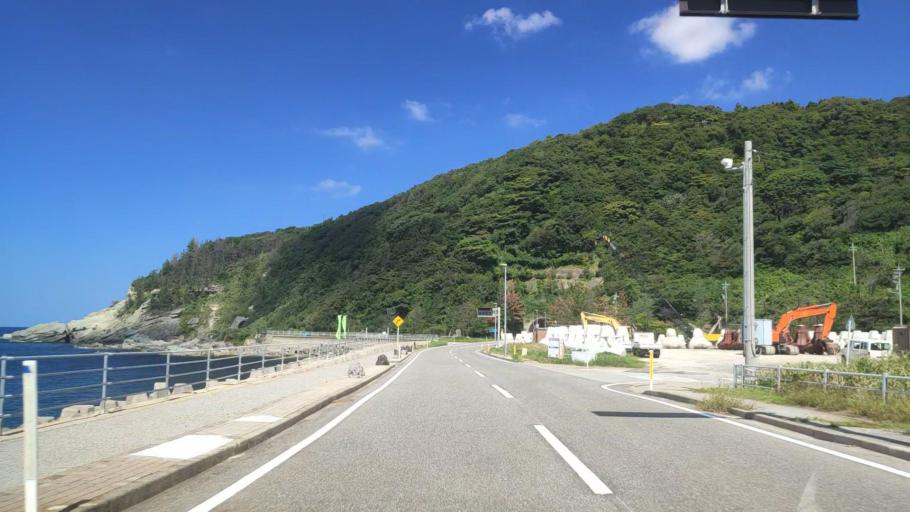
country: JP
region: Ishikawa
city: Nanao
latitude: 37.4727
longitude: 137.0929
